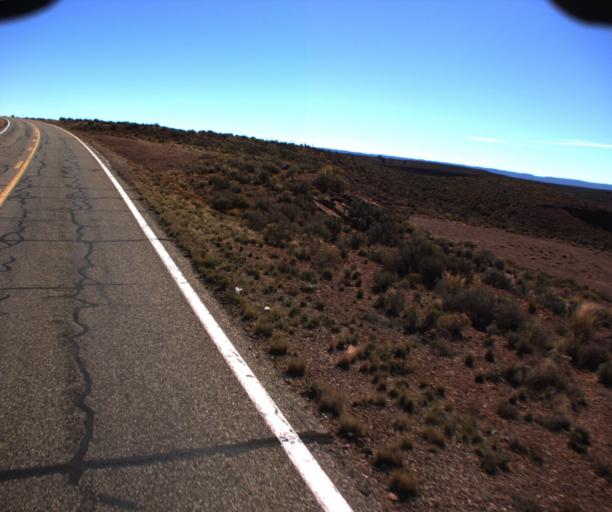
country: US
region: Arizona
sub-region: Coconino County
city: Fredonia
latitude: 36.9086
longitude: -112.4126
